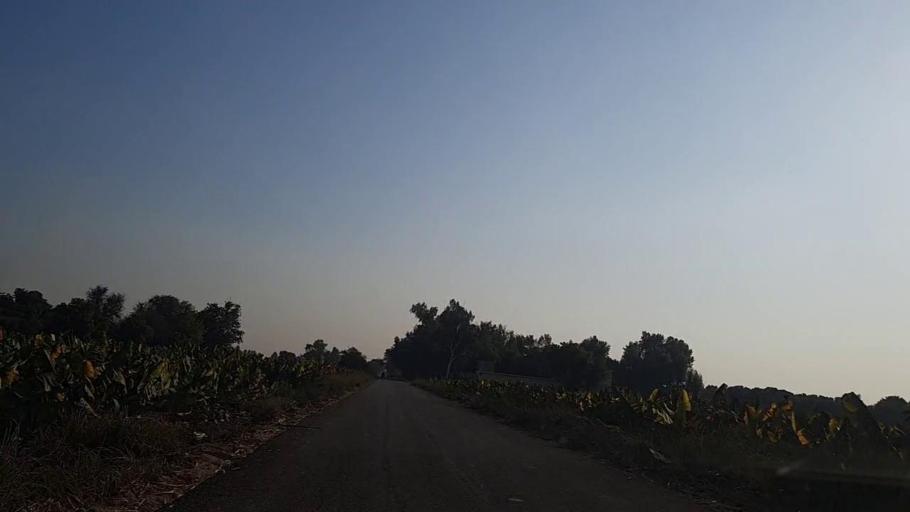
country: PK
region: Sindh
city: Daur
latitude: 26.3325
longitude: 68.1463
